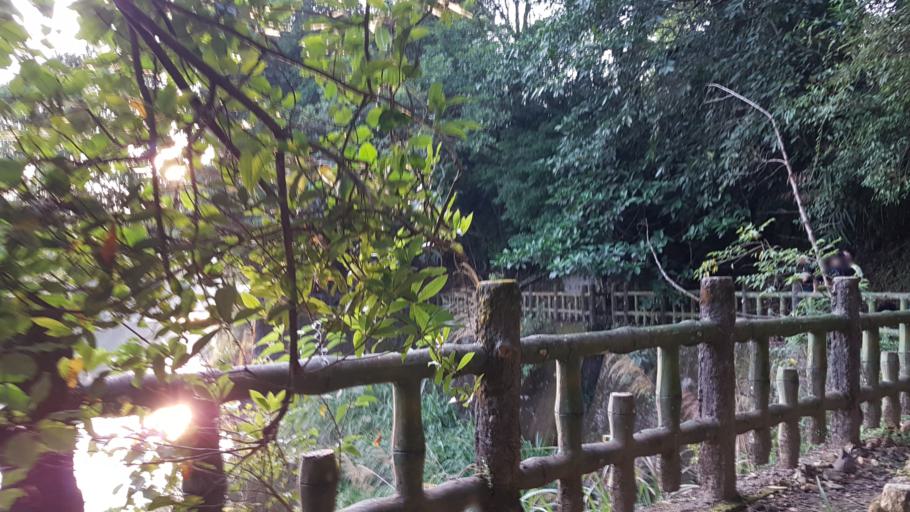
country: TW
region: Taiwan
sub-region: Yilan
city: Yilan
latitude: 24.9333
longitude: 121.7041
